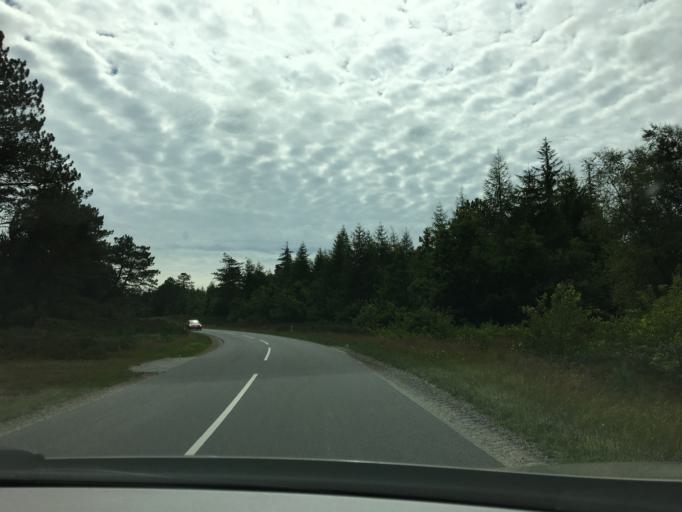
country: DK
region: South Denmark
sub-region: Varde Kommune
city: Oksbol
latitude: 55.7544
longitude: 8.2499
